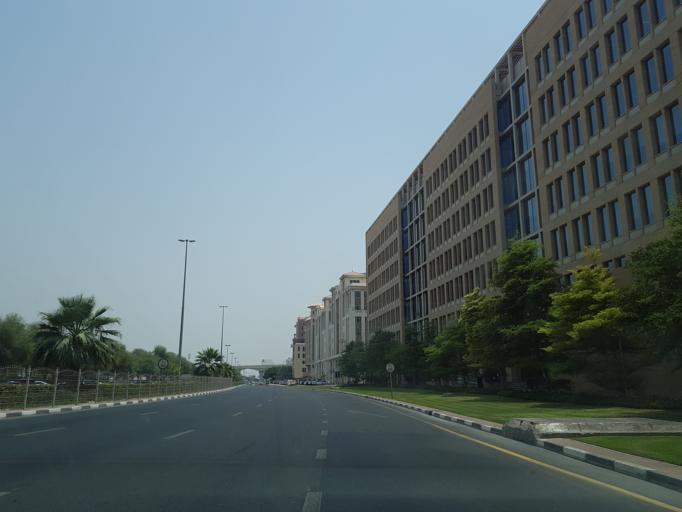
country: AE
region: Ash Shariqah
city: Sharjah
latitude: 25.2344
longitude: 55.3254
